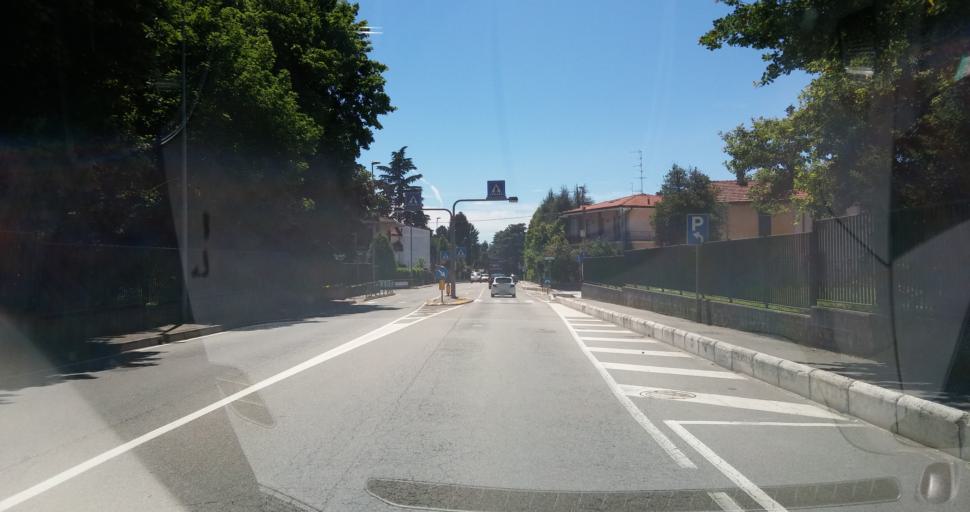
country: IT
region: Lombardy
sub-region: Provincia di Varese
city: Somma Lombardo
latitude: 45.6864
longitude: 8.7020
